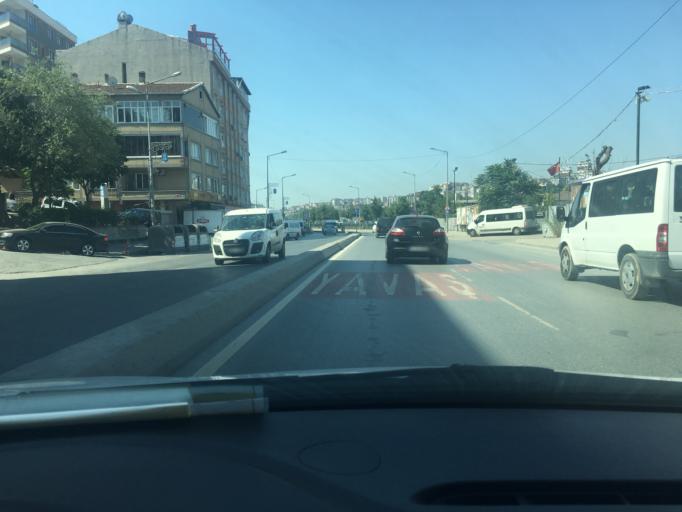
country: TR
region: Istanbul
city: Sisli
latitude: 41.0787
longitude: 28.9508
